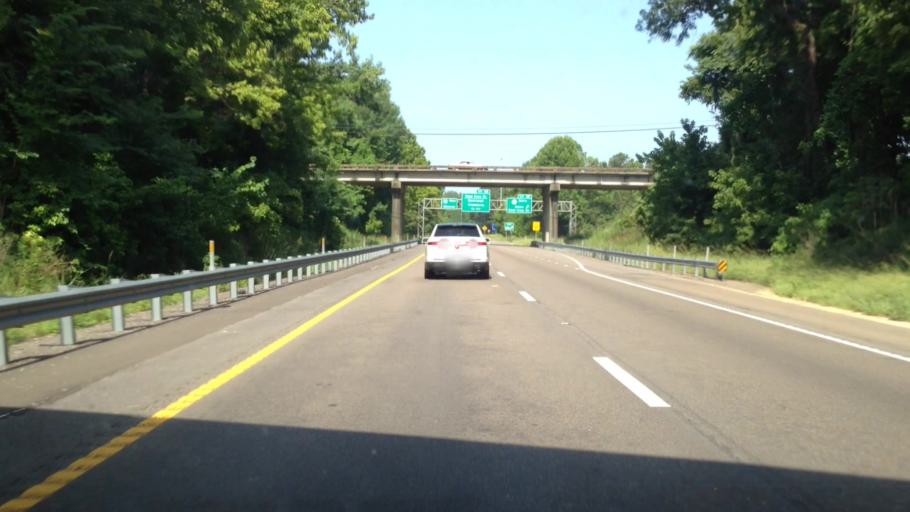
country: US
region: Mississippi
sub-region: Warren County
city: Beechwood
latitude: 32.3485
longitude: -90.8281
